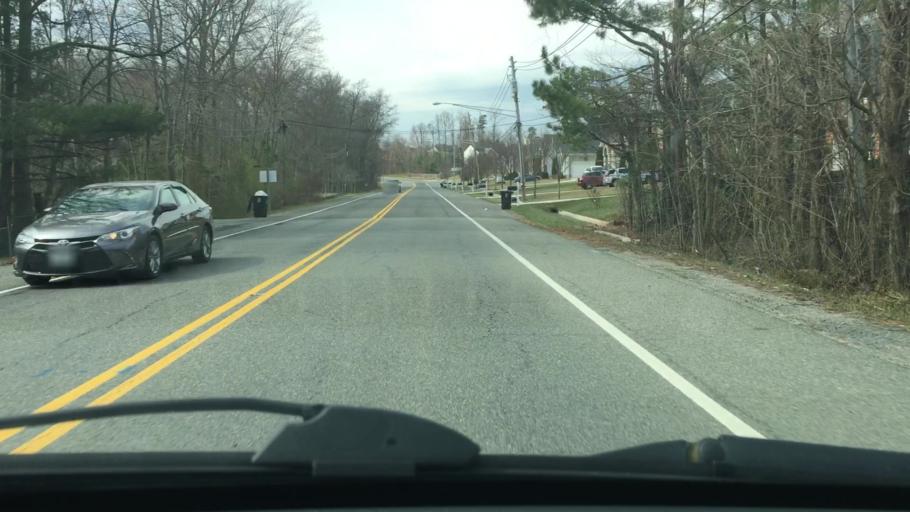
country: US
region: Maryland
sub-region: Prince George's County
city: Glenn Dale
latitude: 38.9935
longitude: -76.8014
